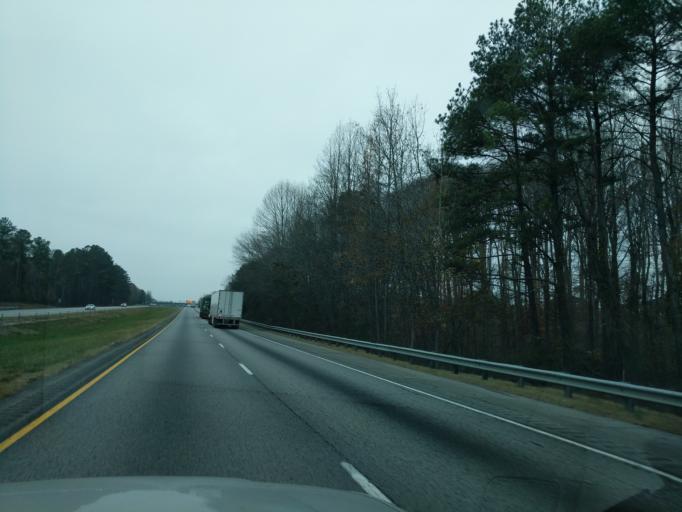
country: US
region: Georgia
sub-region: Franklin County
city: Lavonia
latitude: 34.4261
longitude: -83.1587
